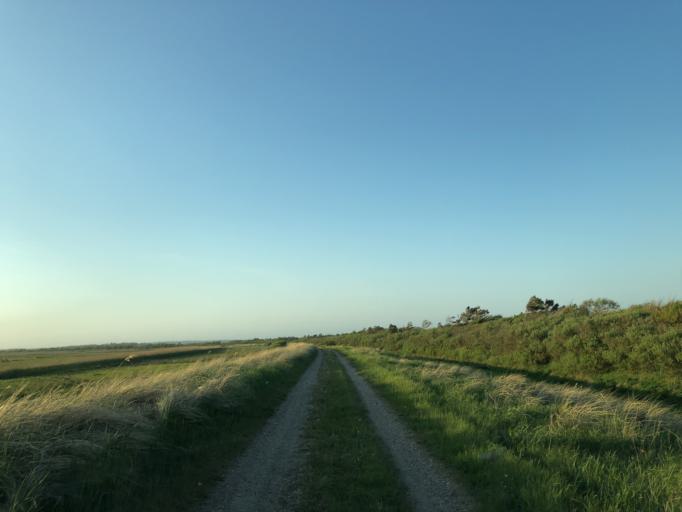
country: DK
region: Central Jutland
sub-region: Holstebro Kommune
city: Ulfborg
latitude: 56.2339
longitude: 8.1674
